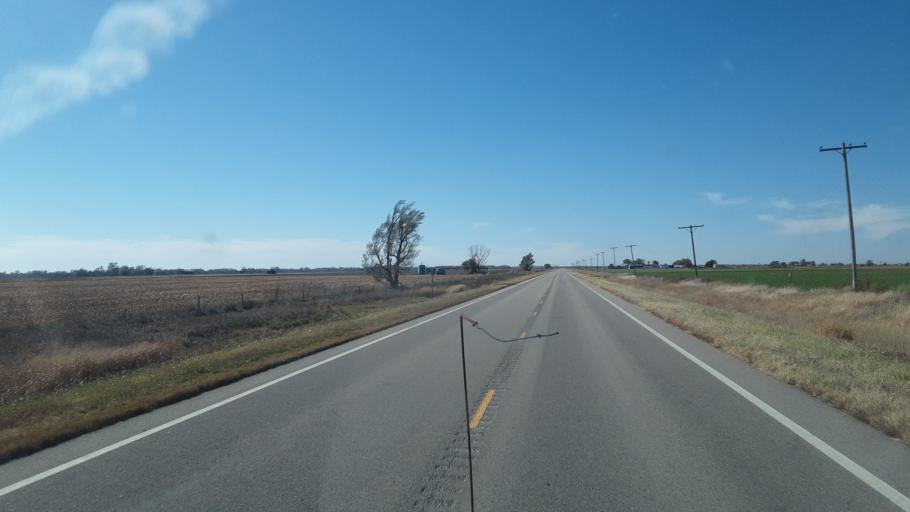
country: US
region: Kansas
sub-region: Barton County
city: Ellinwood
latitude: 38.3471
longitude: -98.5046
